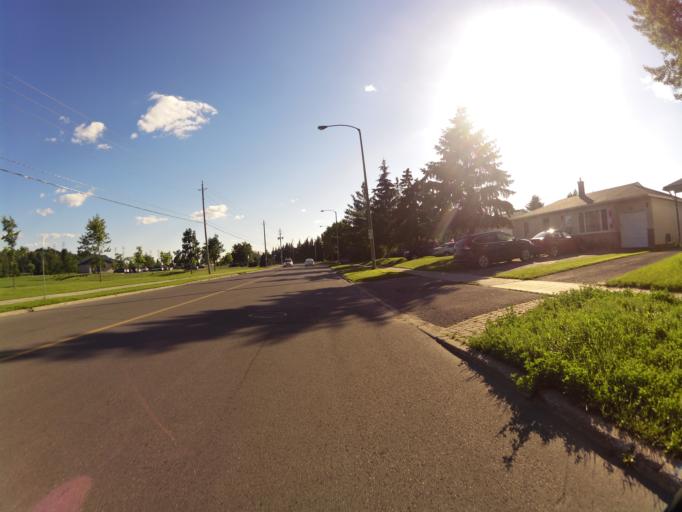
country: CA
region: Ontario
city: Bells Corners
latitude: 45.3271
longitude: -75.7697
